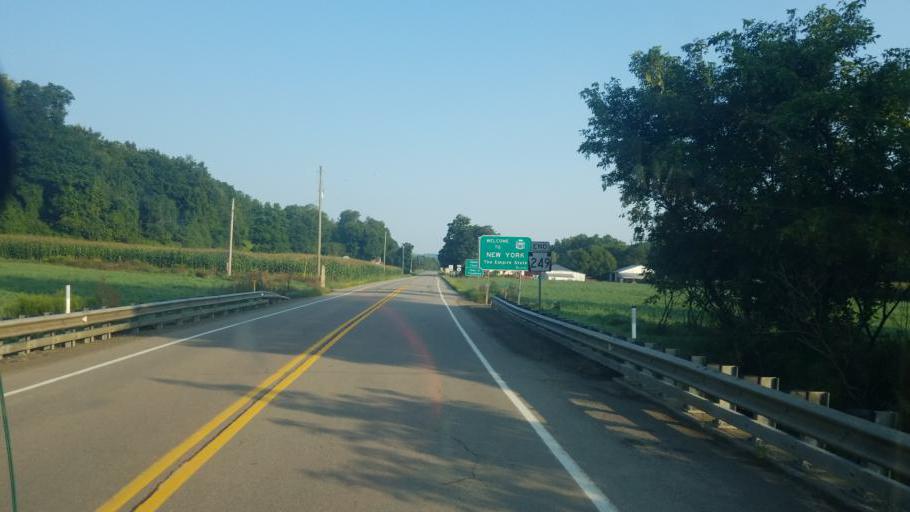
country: US
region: Pennsylvania
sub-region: Tioga County
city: Westfield
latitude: 41.9998
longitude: -77.5036
